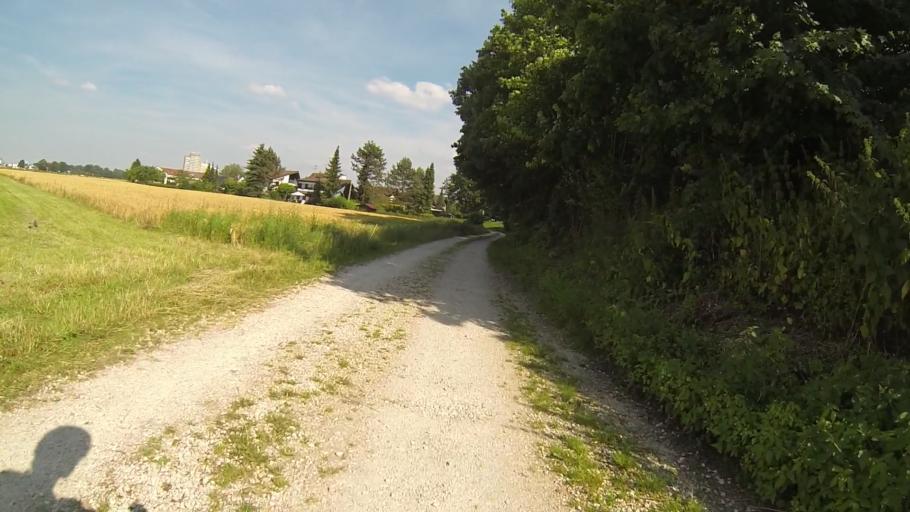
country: DE
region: Bavaria
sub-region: Swabia
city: Neu-Ulm
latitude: 48.3711
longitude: 10.0010
